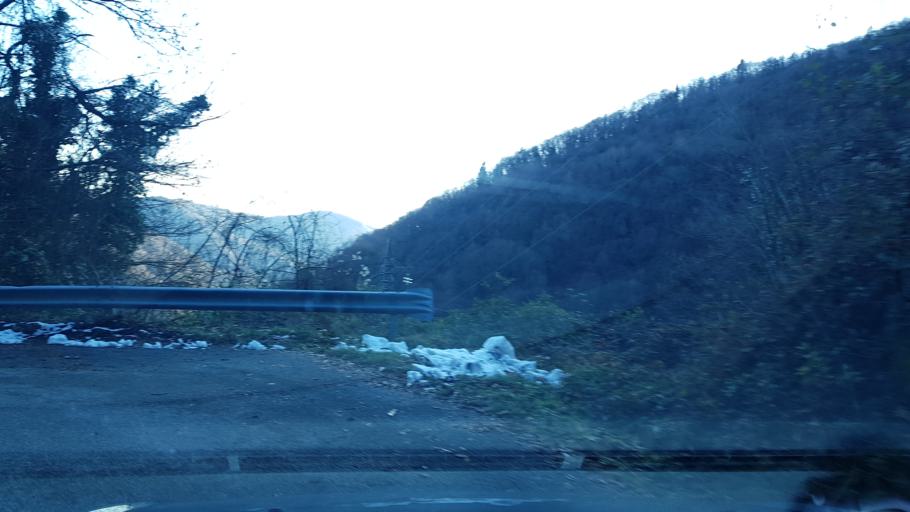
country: IT
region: Friuli Venezia Giulia
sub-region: Provincia di Udine
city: Savogna
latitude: 46.1827
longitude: 13.5352
